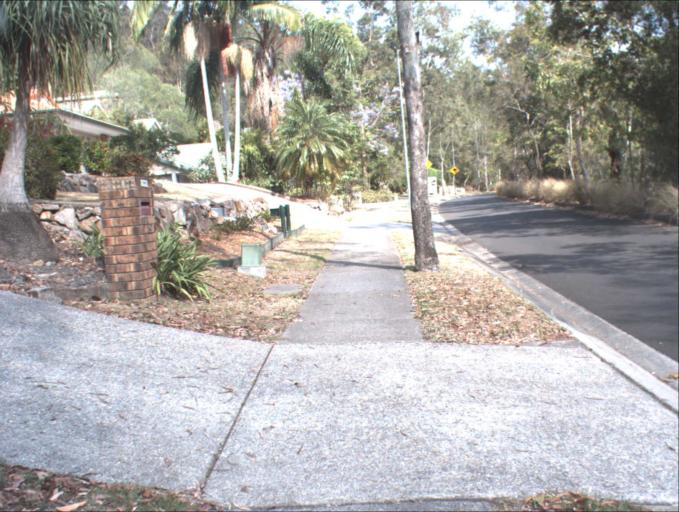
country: AU
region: Queensland
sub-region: Logan
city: Slacks Creek
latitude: -27.6570
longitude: 153.1962
